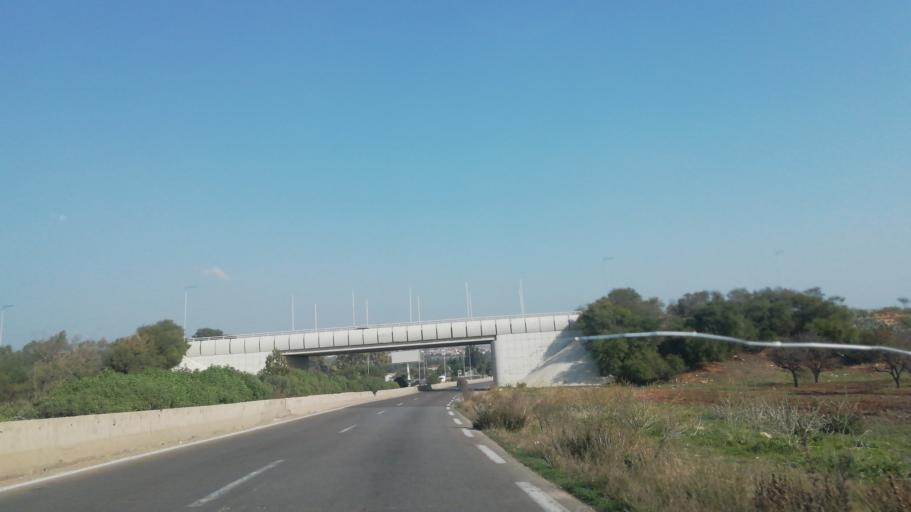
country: DZ
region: Oran
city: Bou Tlelis
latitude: 35.5712
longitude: -0.8820
